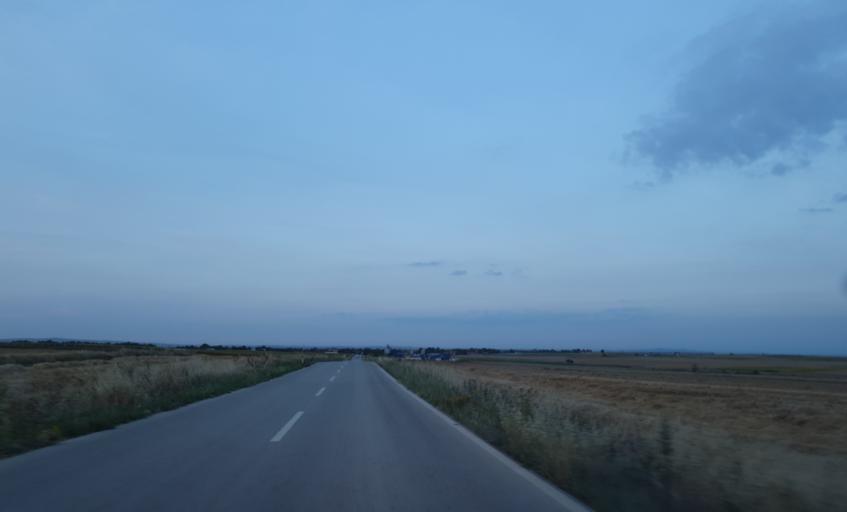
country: TR
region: Tekirdag
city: Beyazkoy
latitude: 41.4281
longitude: 27.6820
